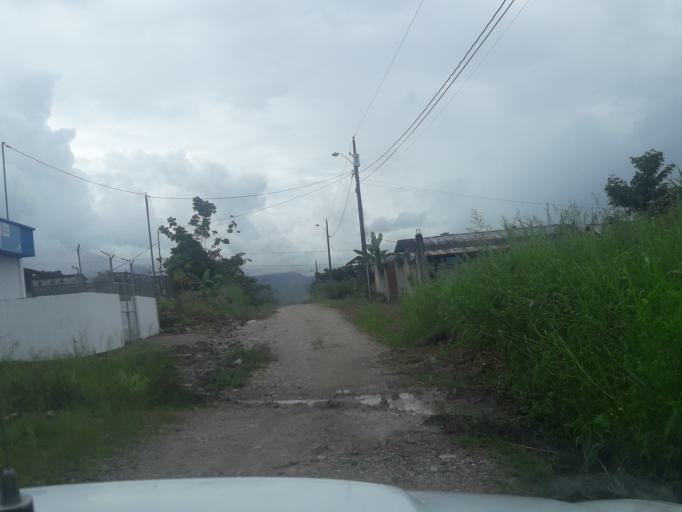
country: EC
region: Napo
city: Archidona
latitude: -0.9476
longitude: -77.8153
